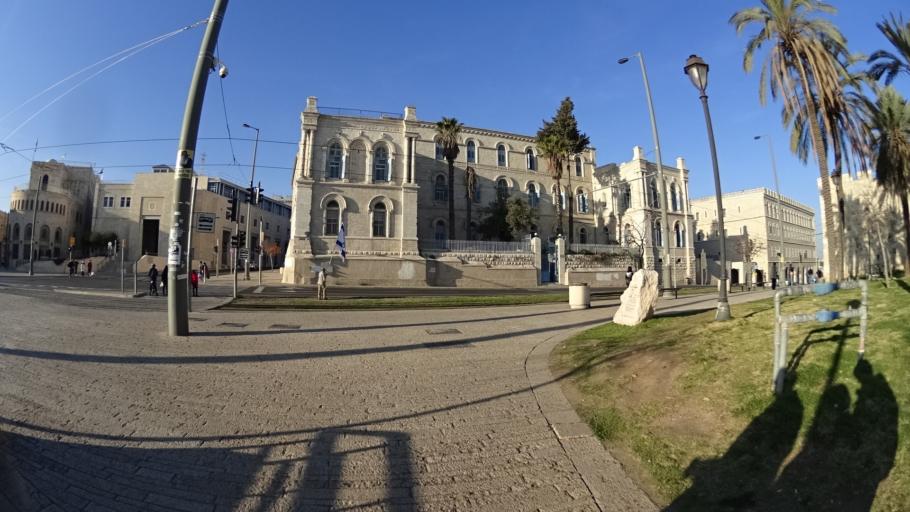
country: IL
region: Jerusalem
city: West Jerusalem
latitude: 31.7789
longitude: 35.2256
